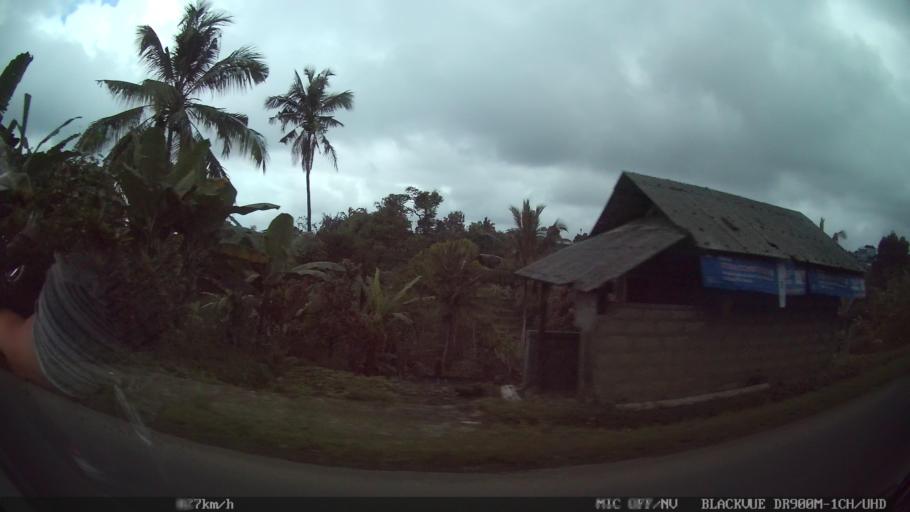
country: ID
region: Bali
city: Empalan
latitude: -8.3856
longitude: 115.1504
